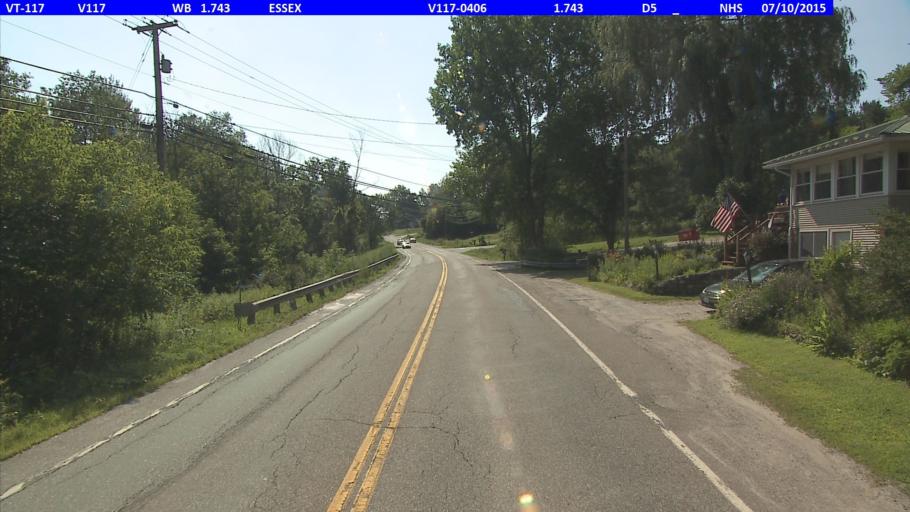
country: US
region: Vermont
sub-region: Chittenden County
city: Essex Junction
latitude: 44.4834
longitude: -73.0777
